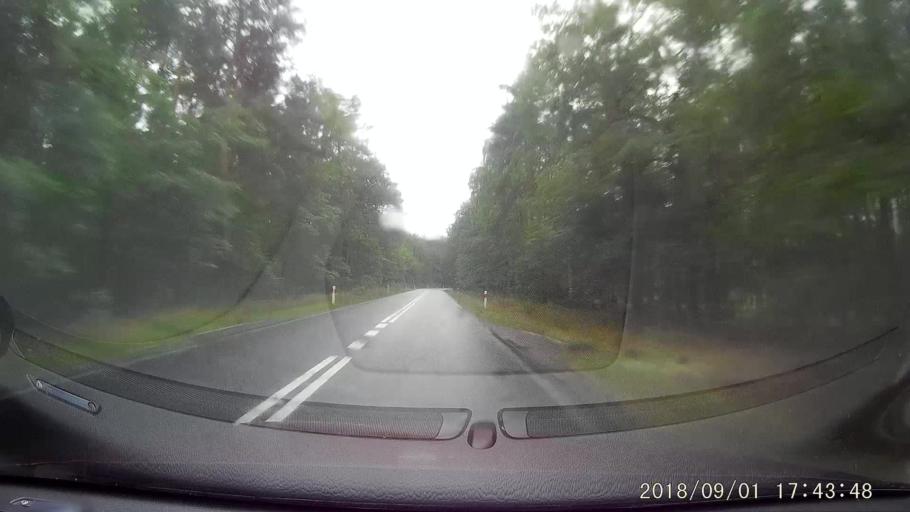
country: PL
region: Lubusz
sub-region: Powiat zaganski
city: Ilowa
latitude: 51.5401
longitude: 15.2459
